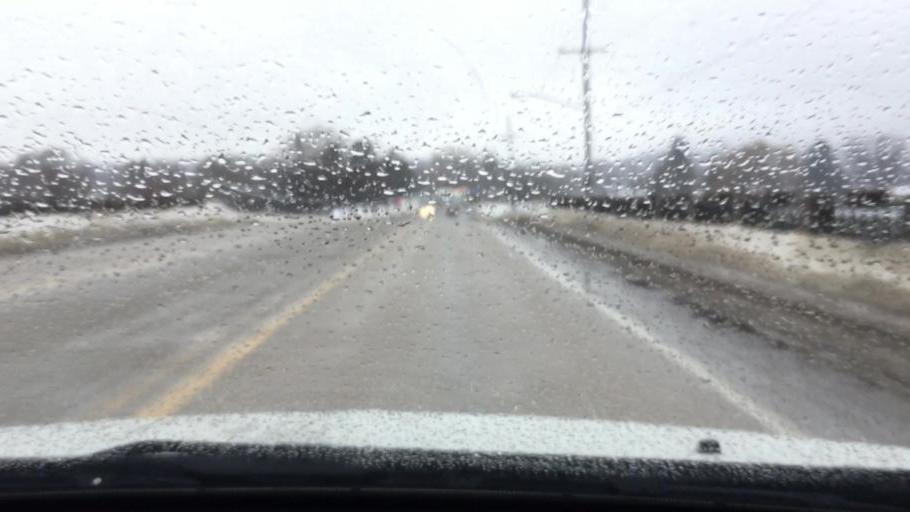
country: US
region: Michigan
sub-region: Charlevoix County
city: East Jordan
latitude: 45.1539
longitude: -85.1293
